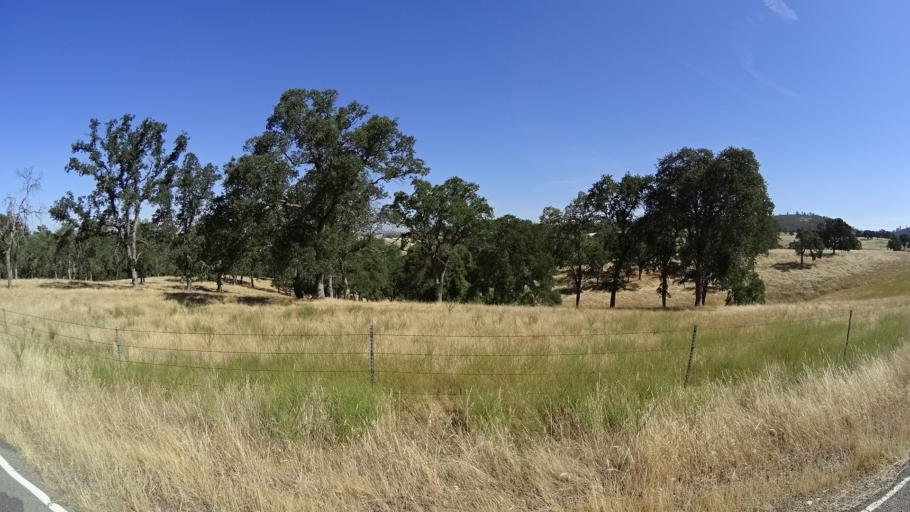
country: US
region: California
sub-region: Calaveras County
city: Valley Springs
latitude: 38.2262
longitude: -120.8235
